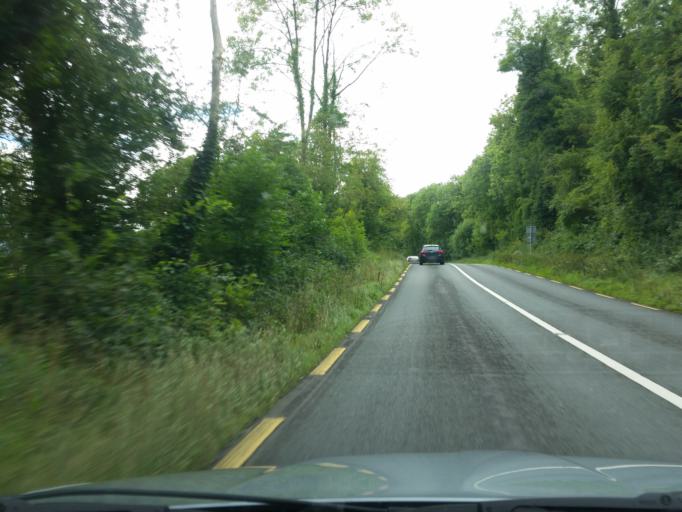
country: IE
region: Ulster
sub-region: An Cabhan
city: Belturbet
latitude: 54.1075
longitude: -7.3605
